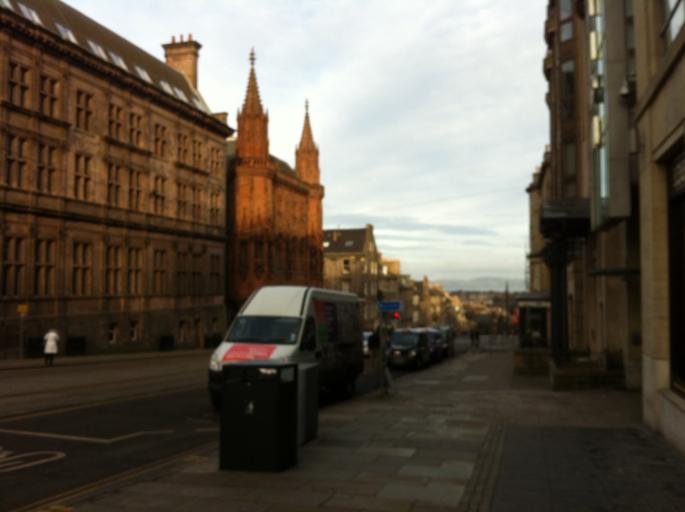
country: GB
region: Scotland
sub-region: Edinburgh
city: Edinburgh
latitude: 55.9551
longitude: -3.1923
